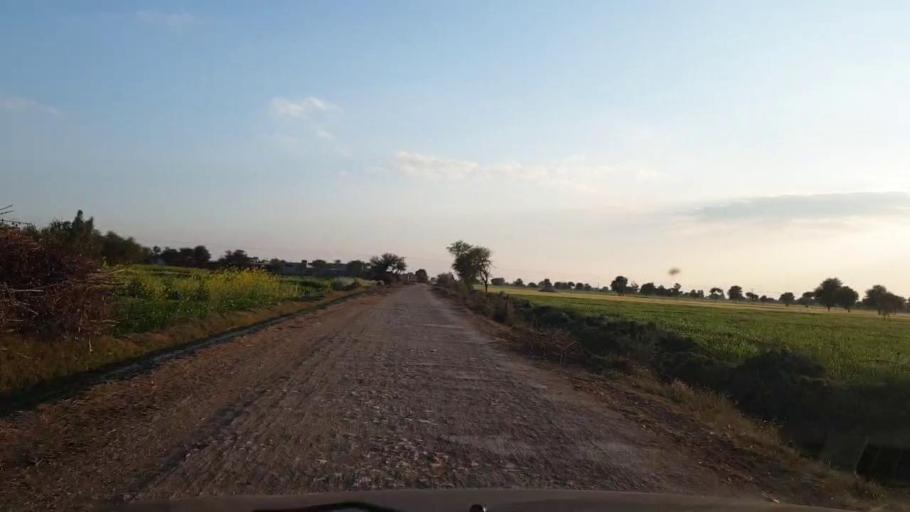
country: PK
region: Sindh
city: Sinjhoro
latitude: 25.9998
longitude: 68.8014
